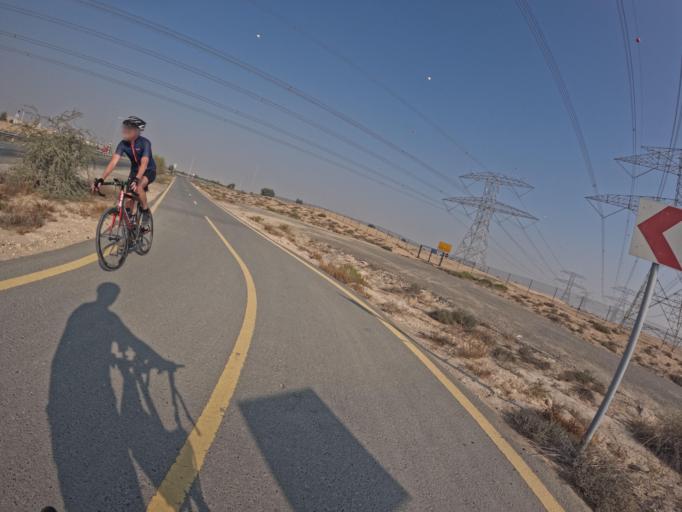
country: AE
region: Dubai
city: Dubai
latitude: 25.0520
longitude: 55.3141
